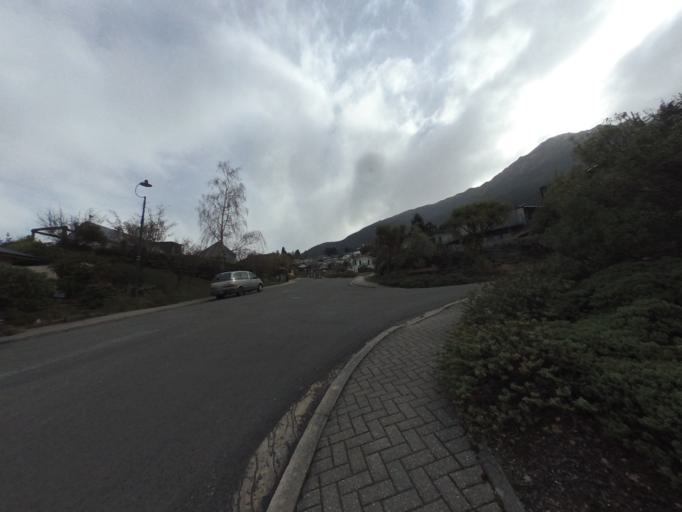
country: NZ
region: Otago
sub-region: Queenstown-Lakes District
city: Queenstown
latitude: -45.0402
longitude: 168.6358
